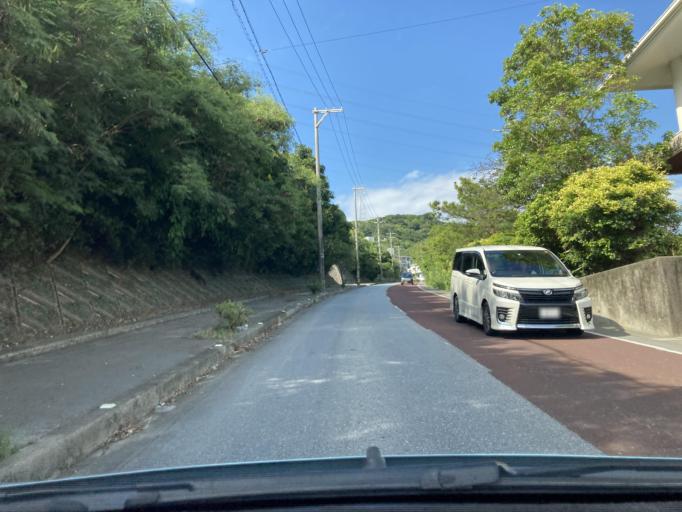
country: JP
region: Okinawa
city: Ginowan
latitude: 26.2744
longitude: 127.7969
